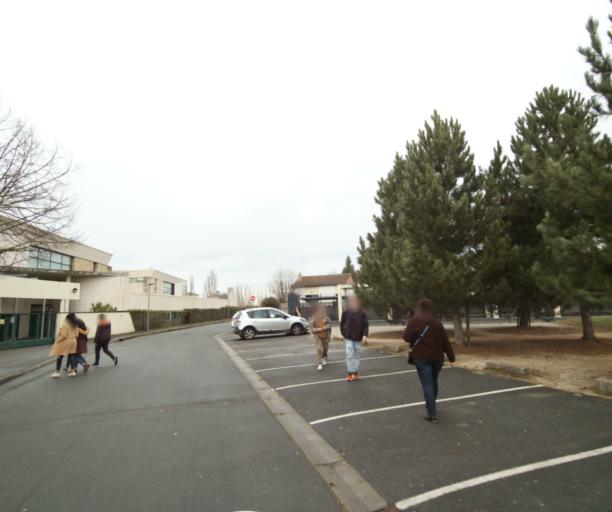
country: FR
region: Poitou-Charentes
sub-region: Departement des Deux-Sevres
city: Niort
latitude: 46.3314
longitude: -0.4685
